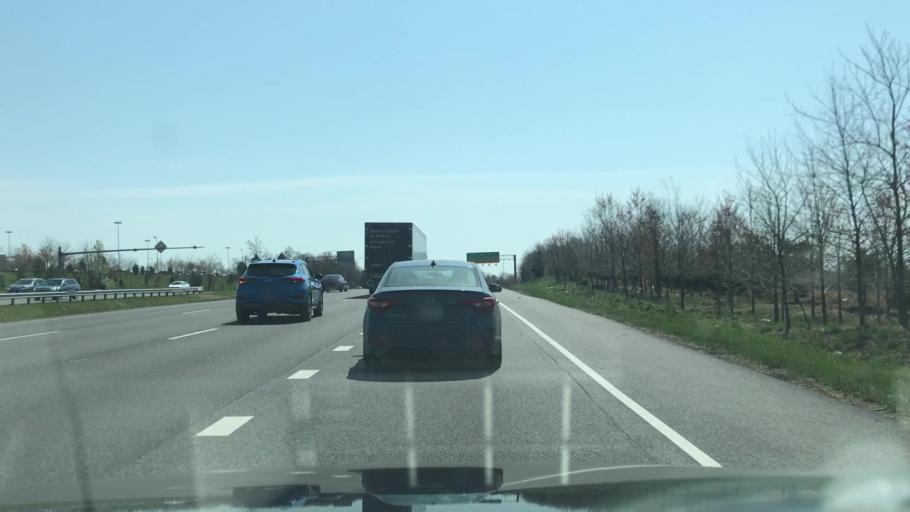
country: US
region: Maryland
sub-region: Anne Arundel County
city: Jessup
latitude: 39.1832
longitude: -76.7963
